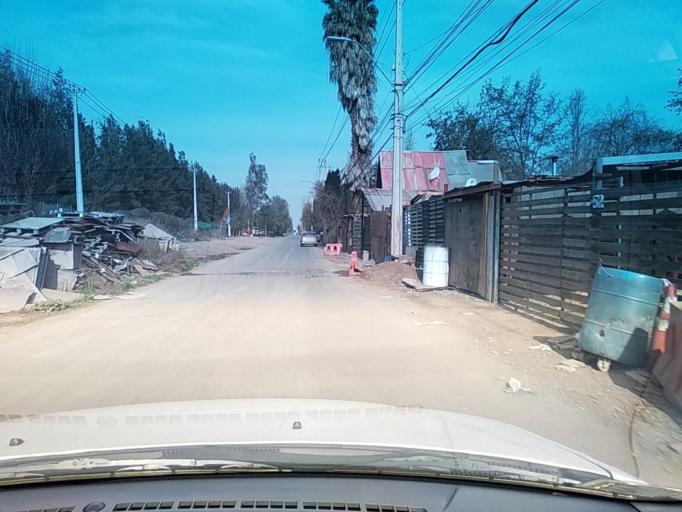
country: CL
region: Santiago Metropolitan
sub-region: Provincia de Chacabuco
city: Chicureo Abajo
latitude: -33.2903
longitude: -70.7268
